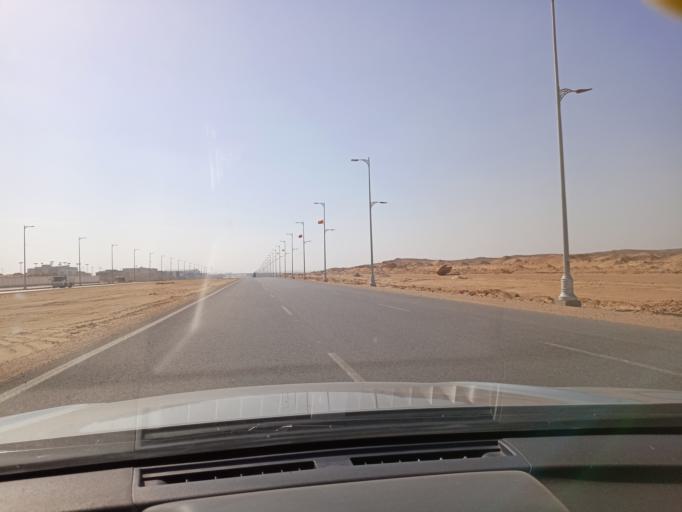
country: EG
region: Muhafazat al Qalyubiyah
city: Al Khankah
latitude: 30.0444
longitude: 31.7071
